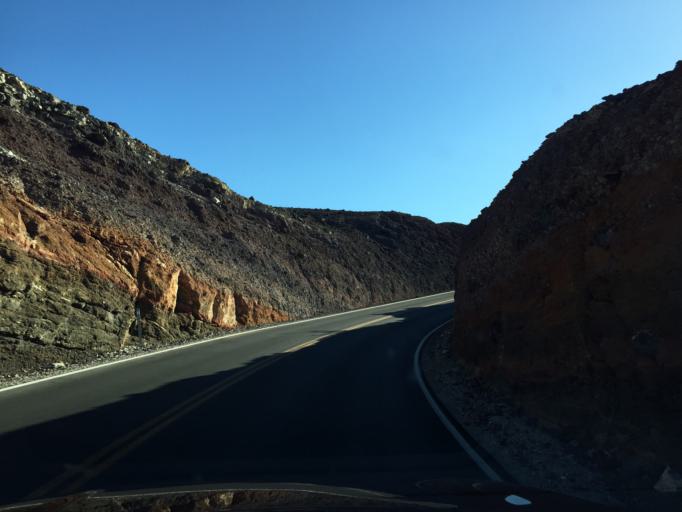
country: US
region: California
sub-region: San Bernardino County
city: Searles Valley
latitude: 36.3423
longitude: -117.5060
